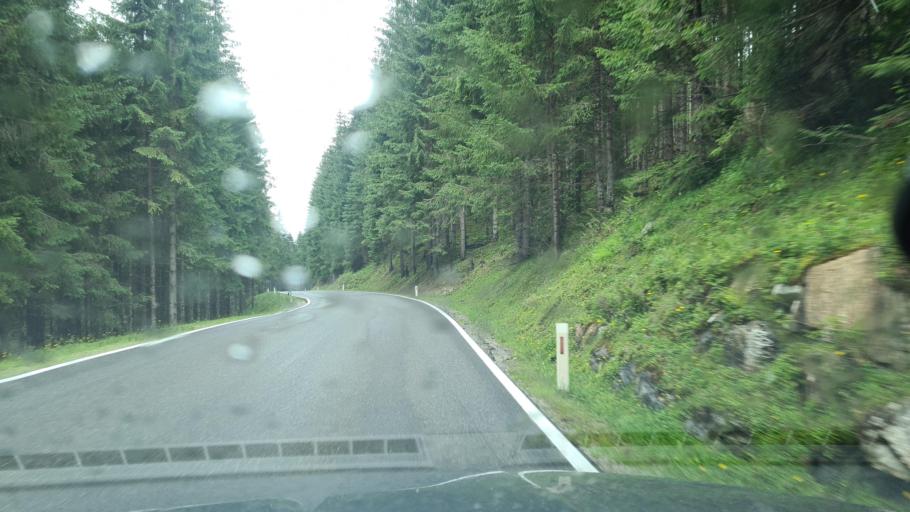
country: AT
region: Salzburg
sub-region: Politischer Bezirk Sankt Johann im Pongau
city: Untertauern
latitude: 47.3197
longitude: 13.4471
